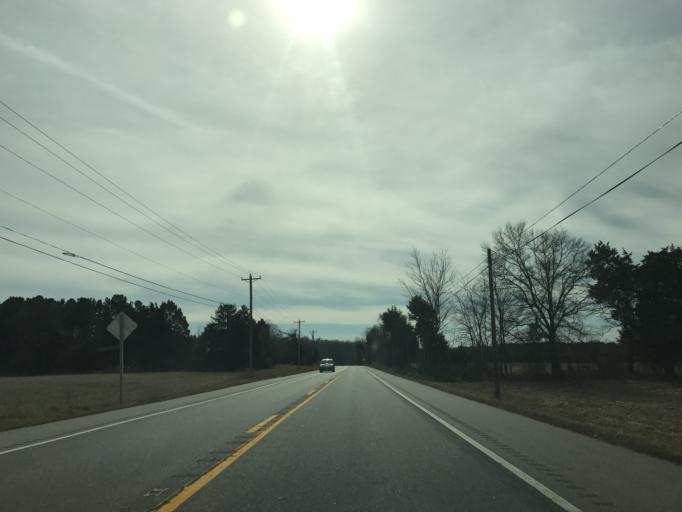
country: US
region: Maryland
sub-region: Queen Anne's County
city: Centreville
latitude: 39.1136
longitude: -76.0230
